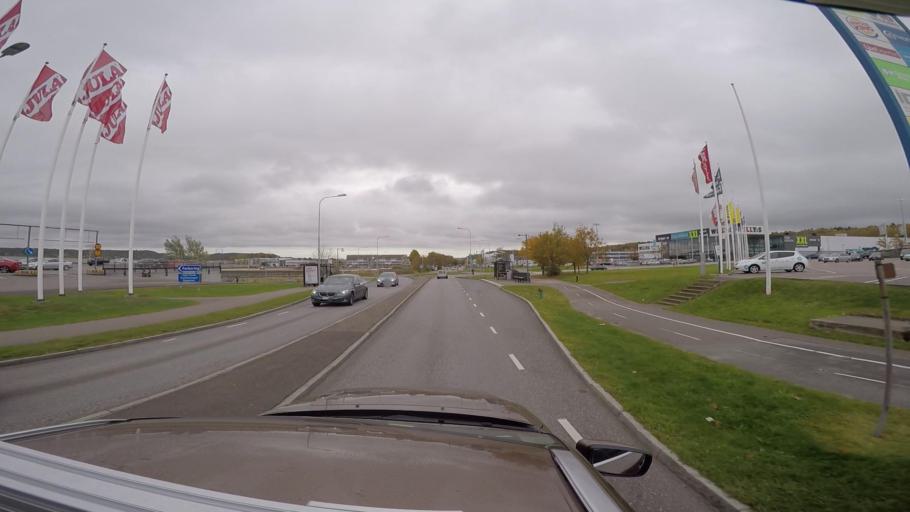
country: SE
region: Vaestra Goetaland
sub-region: Goteborg
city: Majorna
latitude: 57.6414
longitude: 11.9499
